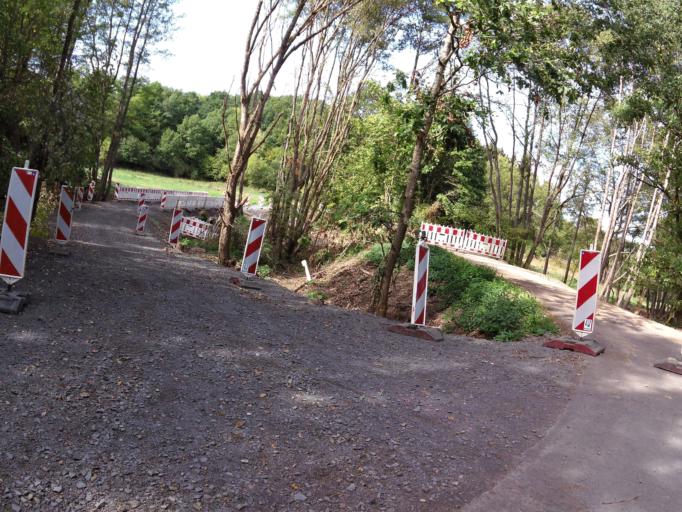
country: DE
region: Rheinland-Pfalz
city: Pronsfeld
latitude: 50.1498
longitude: 6.3376
